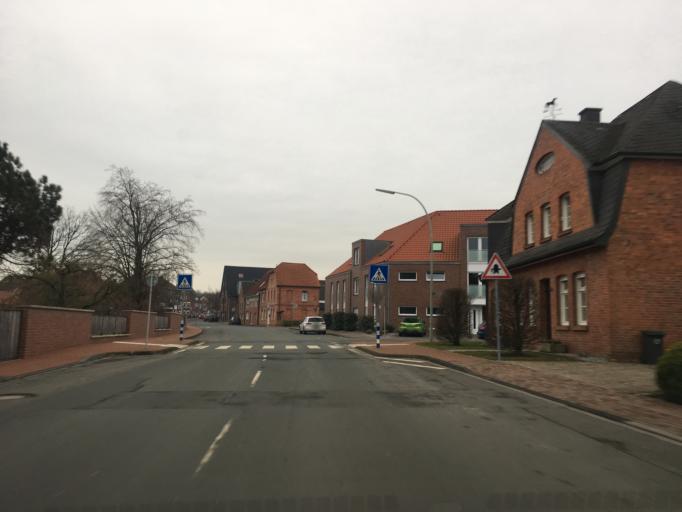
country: DE
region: North Rhine-Westphalia
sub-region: Regierungsbezirk Munster
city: Nordkirchen
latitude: 51.7393
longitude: 7.5229
